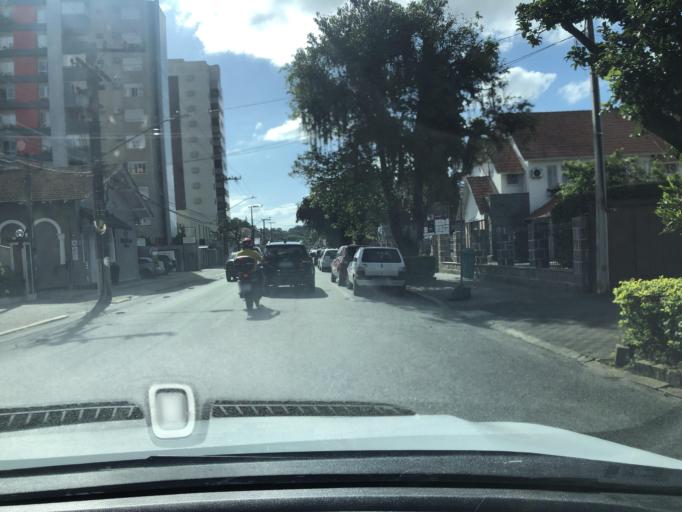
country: BR
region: Santa Catarina
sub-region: Joinville
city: Joinville
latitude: -26.2969
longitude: -48.8485
